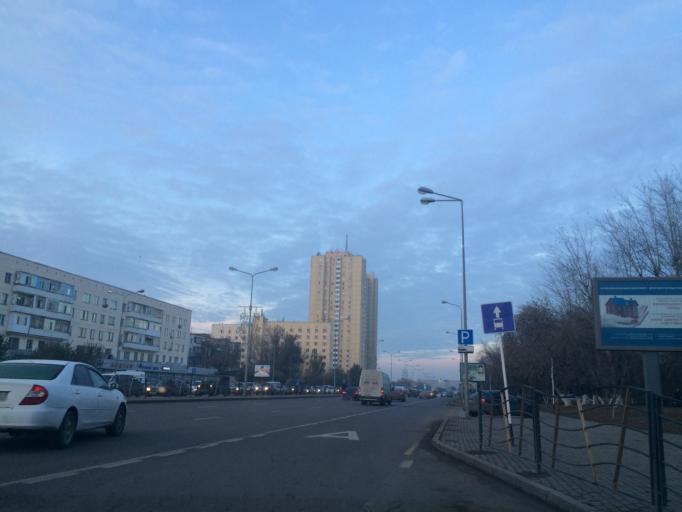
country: KZ
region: Astana Qalasy
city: Astana
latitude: 51.1759
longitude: 71.4105
